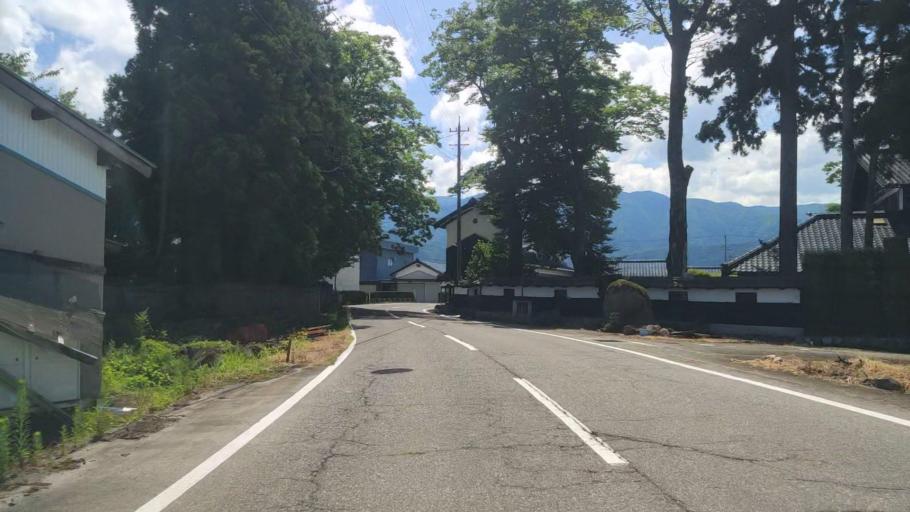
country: JP
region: Fukui
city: Ono
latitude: 35.9612
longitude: 136.5316
